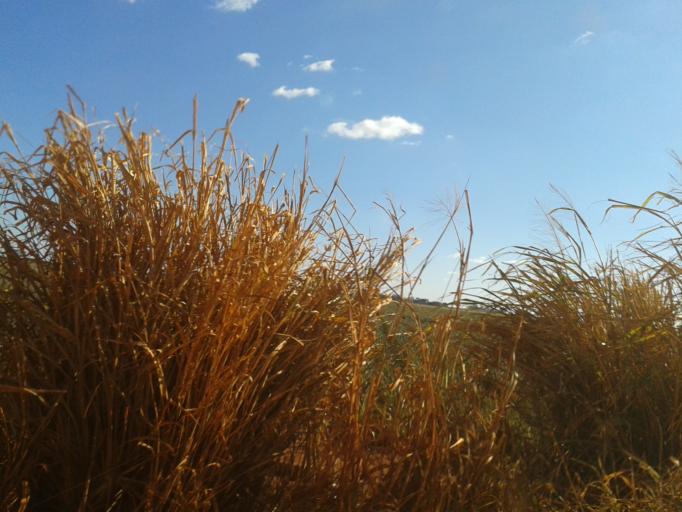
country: BR
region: Minas Gerais
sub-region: Centralina
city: Centralina
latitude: -18.7430
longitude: -49.1893
